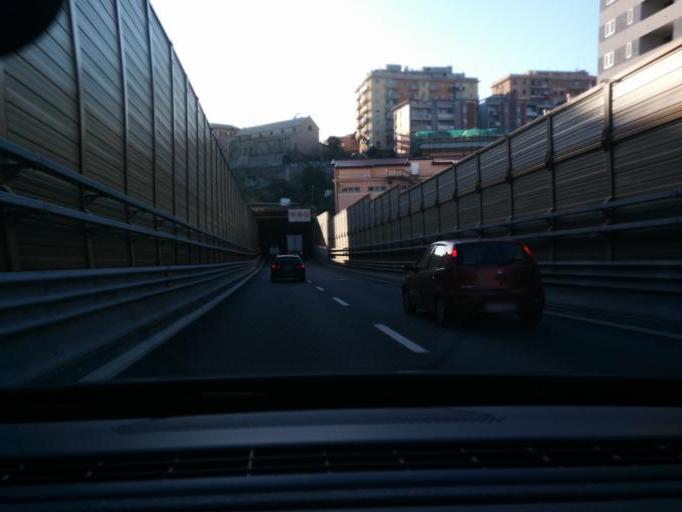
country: IT
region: Liguria
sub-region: Provincia di Genova
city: San Teodoro
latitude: 44.4300
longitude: 8.8544
